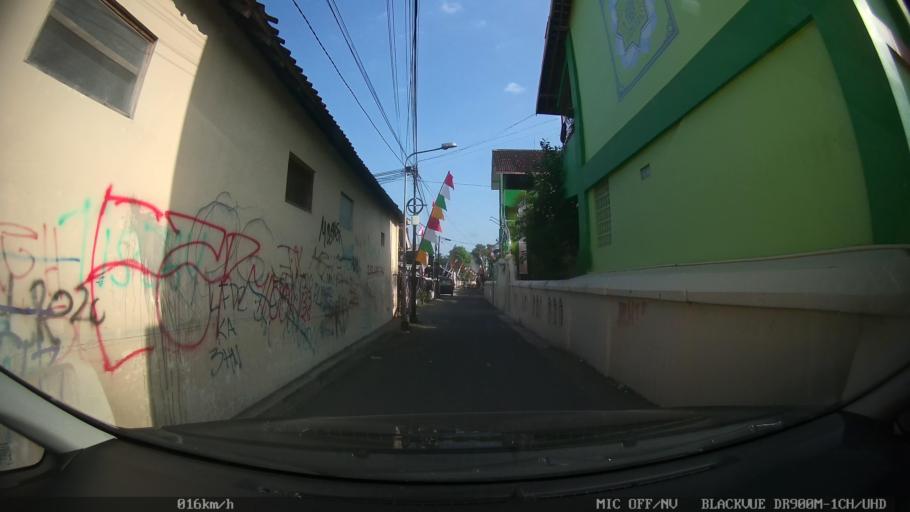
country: ID
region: Daerah Istimewa Yogyakarta
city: Yogyakarta
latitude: -7.7965
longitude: 110.3508
